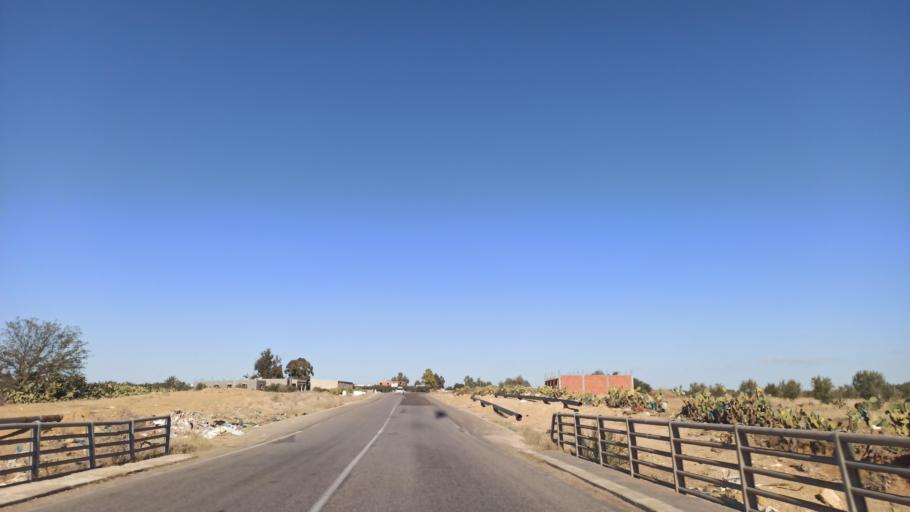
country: TN
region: Sidi Bu Zayd
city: Jilma
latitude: 35.2525
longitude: 9.3979
